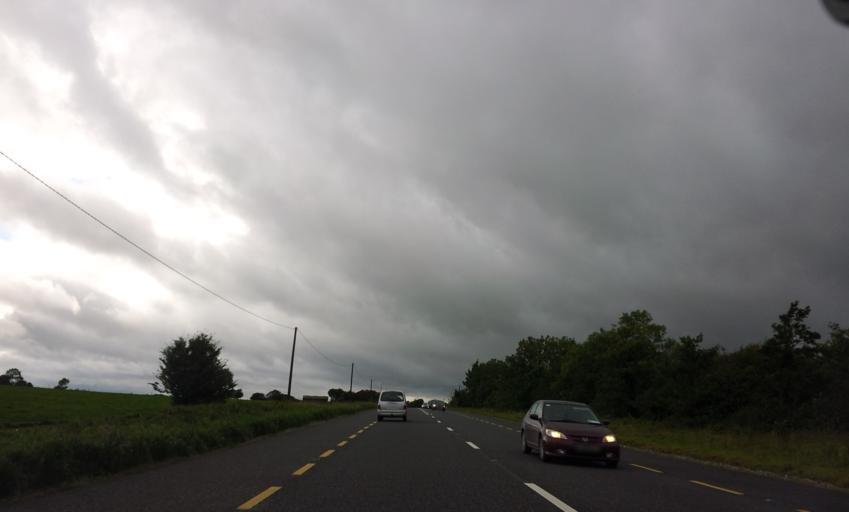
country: IE
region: Munster
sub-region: County Cork
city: Youghal
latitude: 51.9378
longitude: -7.9434
